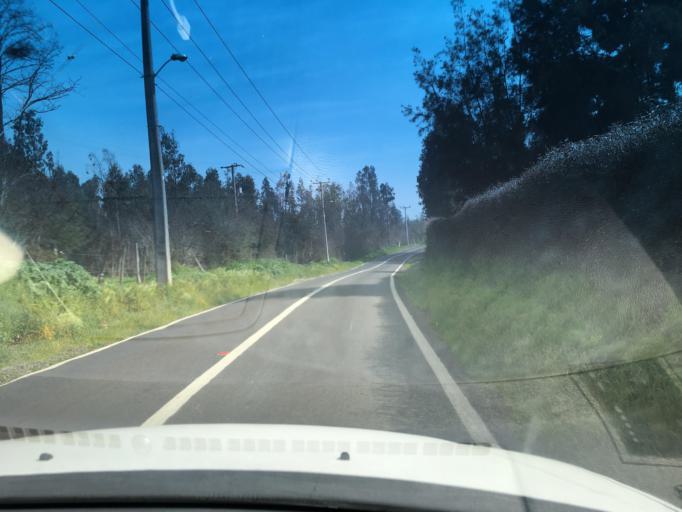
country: CL
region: Valparaiso
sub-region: Provincia de Marga Marga
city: Limache
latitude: -33.0117
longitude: -71.2134
